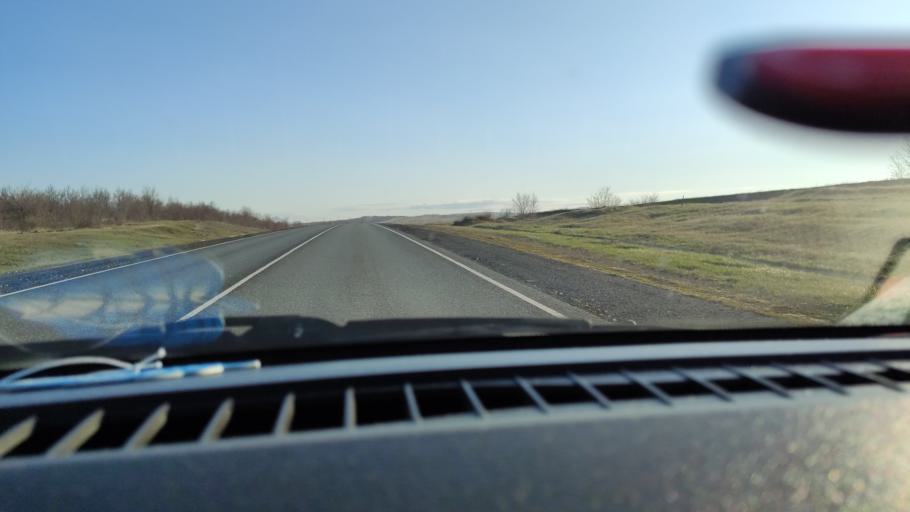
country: RU
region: Saratov
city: Balakovo
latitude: 52.1923
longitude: 47.8548
